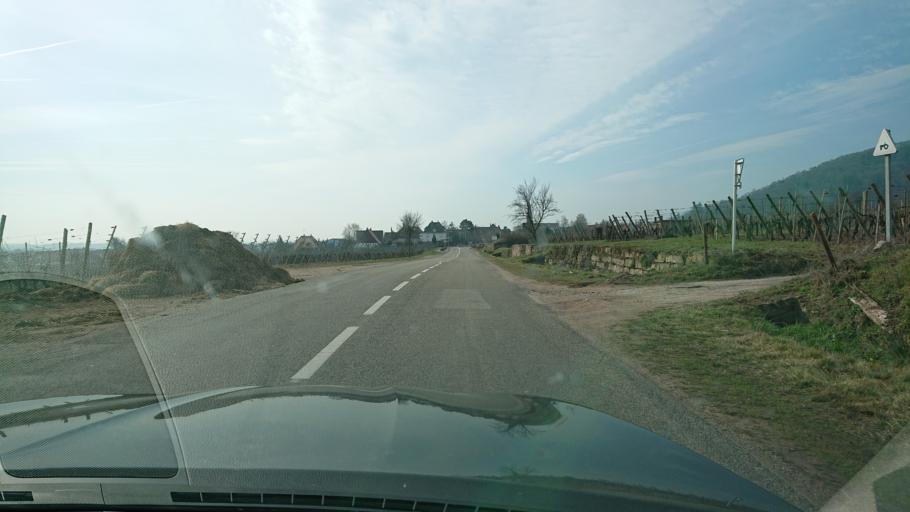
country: FR
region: Alsace
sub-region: Departement du Bas-Rhin
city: Kintzheim
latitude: 48.2611
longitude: 7.3987
